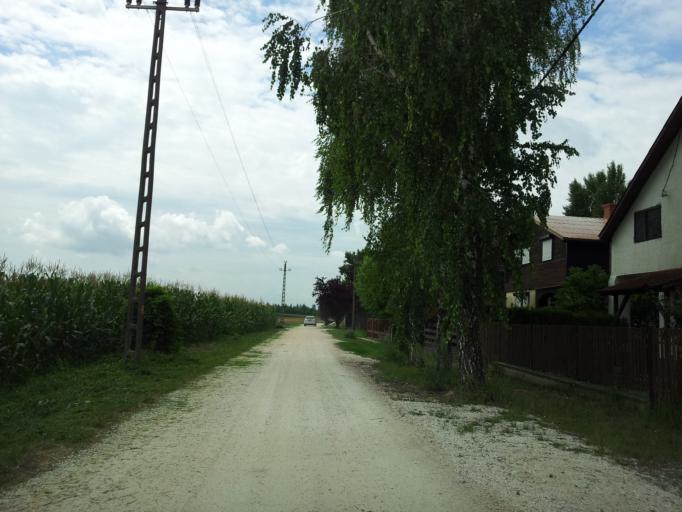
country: HU
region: Pest
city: Szigetcsep
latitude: 47.2353
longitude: 18.9763
